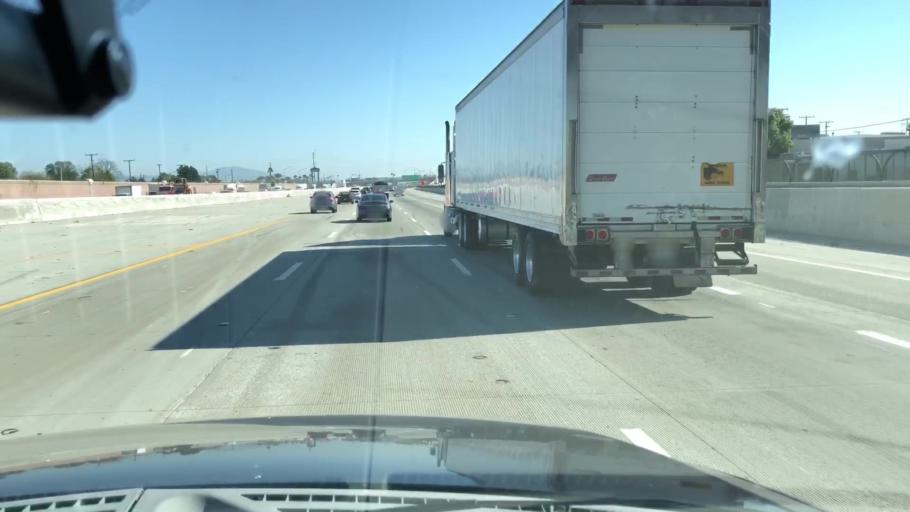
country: US
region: California
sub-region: Los Angeles County
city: Norwalk
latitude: 33.8984
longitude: -118.0555
